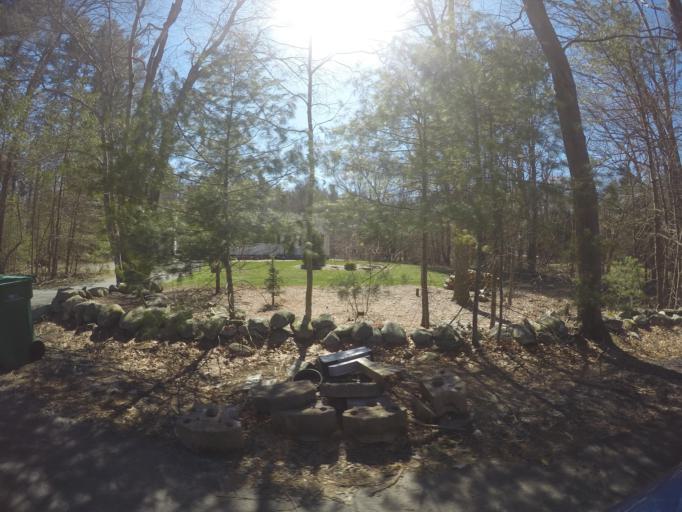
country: US
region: Massachusetts
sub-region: Bristol County
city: Easton
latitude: 41.9949
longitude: -71.1053
